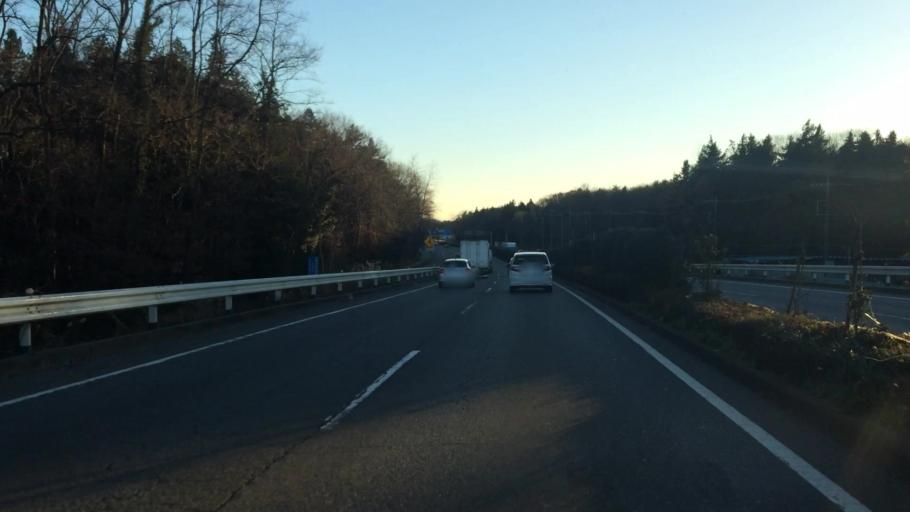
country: JP
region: Tochigi
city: Utsunomiya-shi
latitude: 36.5216
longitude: 139.9203
